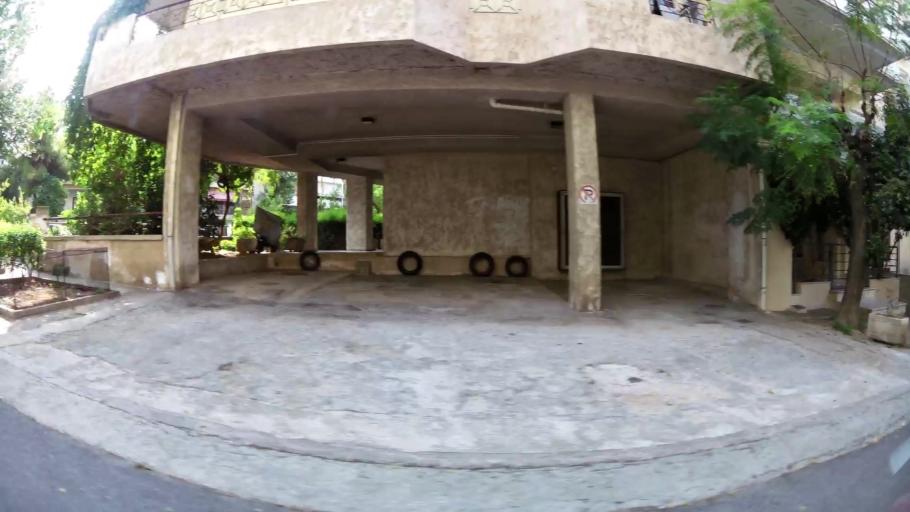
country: GR
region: Attica
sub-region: Nomarchia Athinas
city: Nea Smyrni
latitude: 37.9445
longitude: 23.7077
